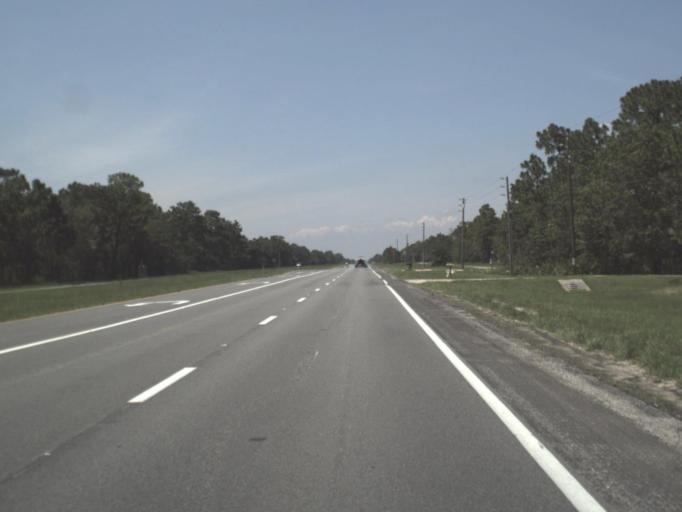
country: US
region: Florida
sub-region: Citrus County
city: Sugarmill Woods
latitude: 28.6642
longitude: -82.5521
